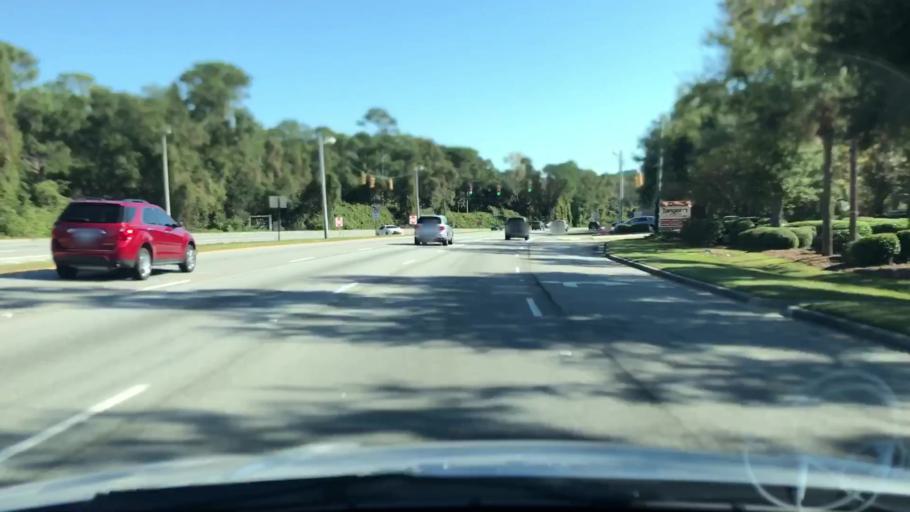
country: US
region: South Carolina
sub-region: Beaufort County
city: Bluffton
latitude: 32.2408
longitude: -80.8175
